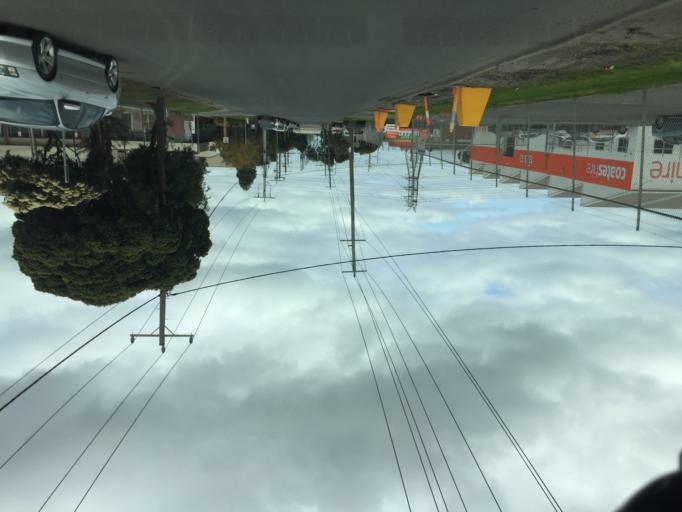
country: AU
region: Victoria
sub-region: Hobsons Bay
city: South Kingsville
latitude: -37.8223
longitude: 144.8596
